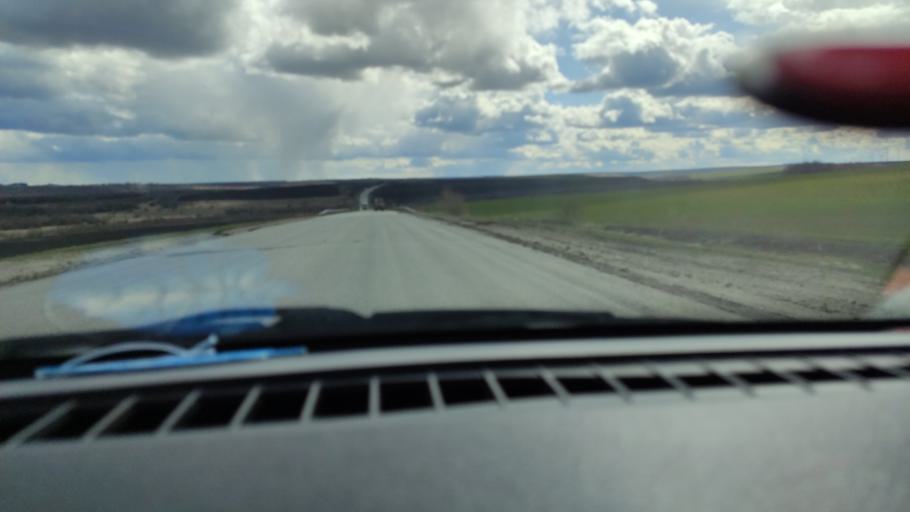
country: RU
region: Samara
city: Varlamovo
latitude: 53.0759
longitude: 48.3541
